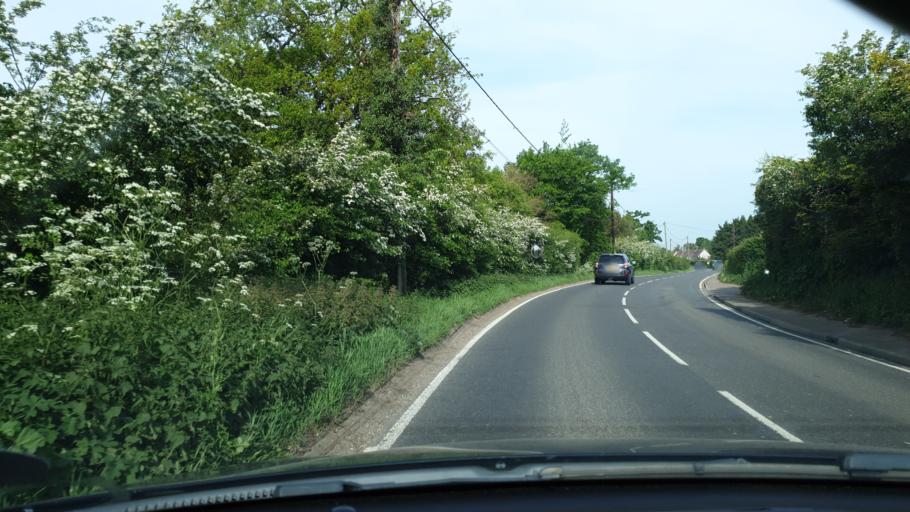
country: GB
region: England
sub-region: Essex
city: Little Clacton
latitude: 51.8534
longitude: 1.1822
